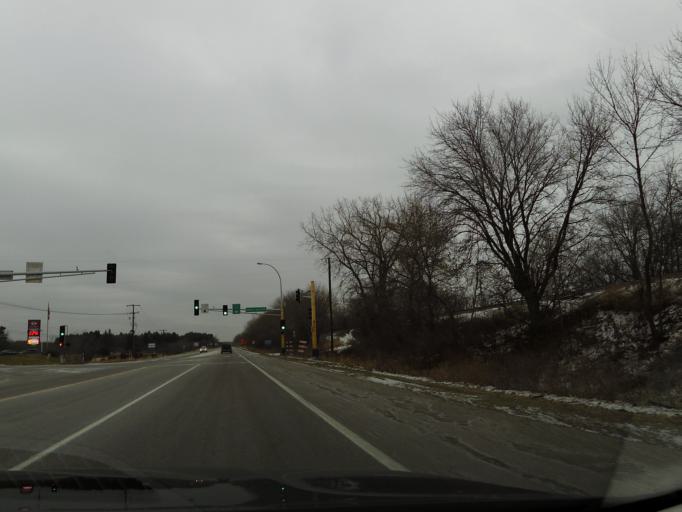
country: US
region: Minnesota
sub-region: Hennepin County
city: Maple Plain
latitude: 45.0037
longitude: -93.6466
